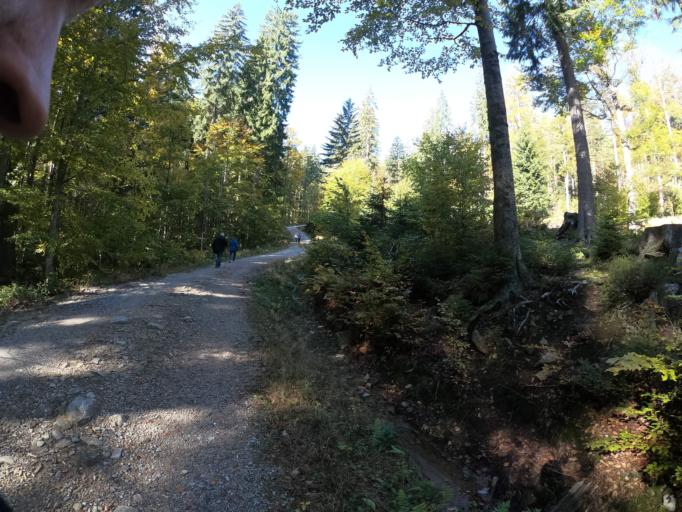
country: DE
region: Bavaria
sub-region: Lower Bavaria
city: Bayerisch Eisenstein
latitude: 49.1021
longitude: 13.1504
